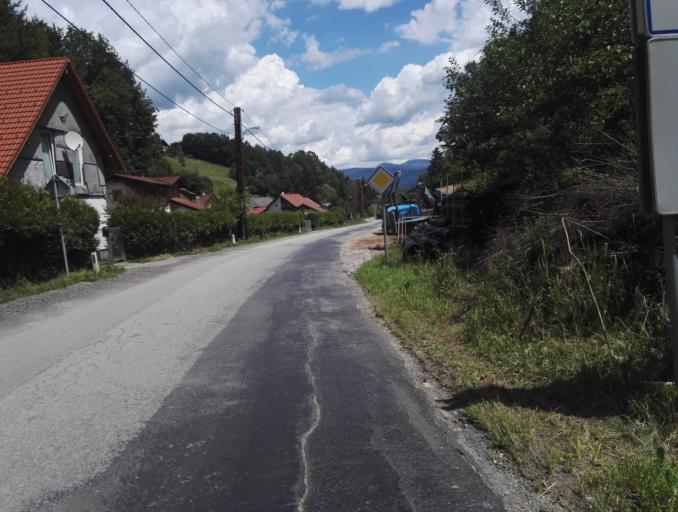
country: AT
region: Styria
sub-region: Politischer Bezirk Graz-Umgebung
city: Gratwein
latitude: 47.1042
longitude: 15.3159
